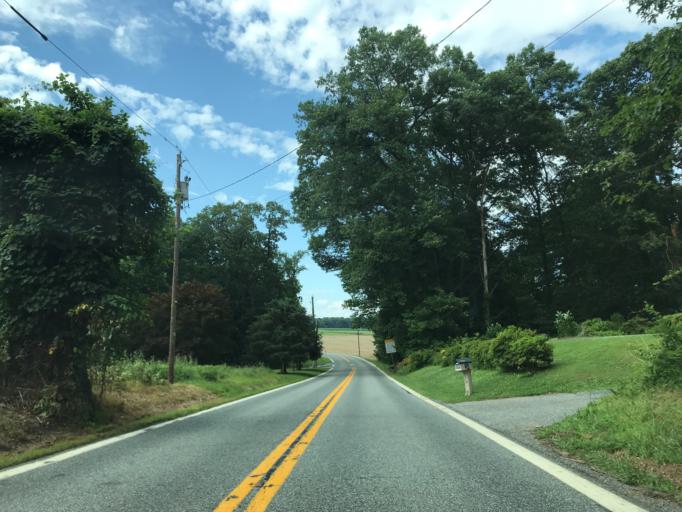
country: US
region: Pennsylvania
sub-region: York County
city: Susquehanna Trails
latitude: 39.7053
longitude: -76.4247
